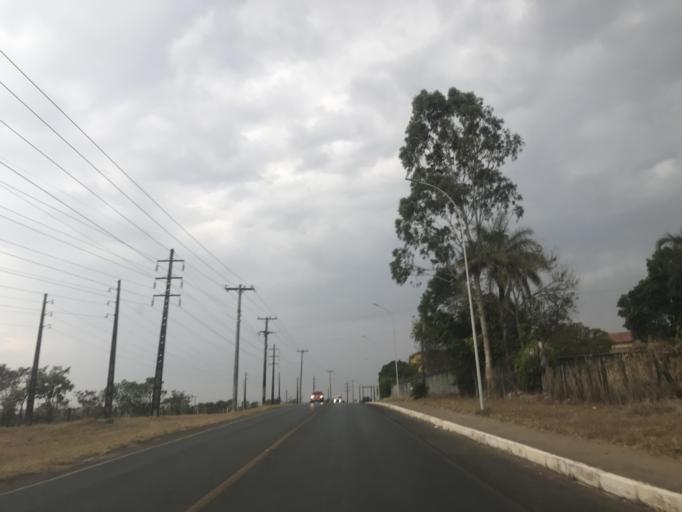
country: BR
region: Federal District
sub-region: Brasilia
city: Brasilia
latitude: -15.6642
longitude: -47.8235
